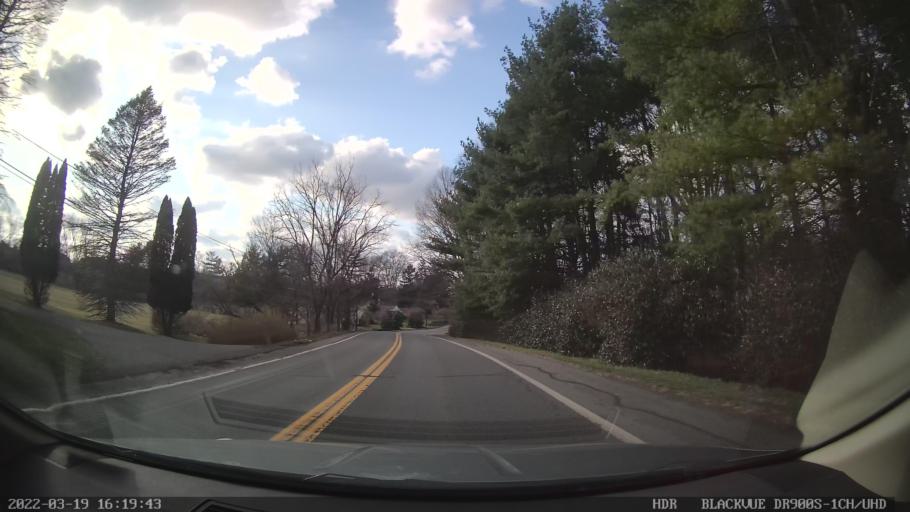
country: US
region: Pennsylvania
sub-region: Lehigh County
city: Dorneyville
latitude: 40.5737
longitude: -75.4994
